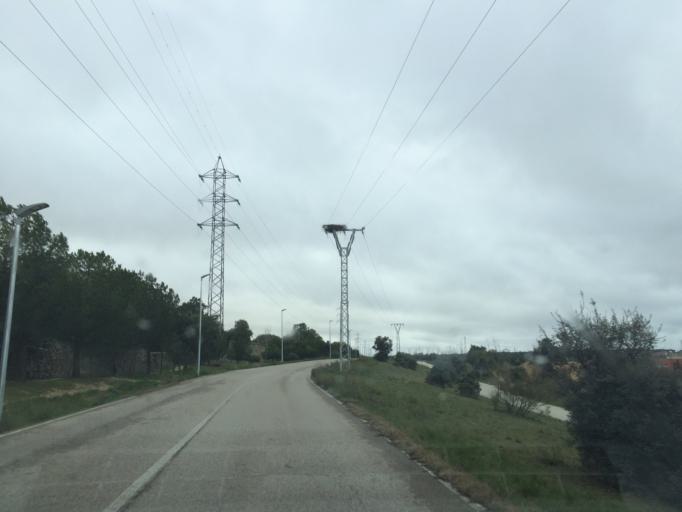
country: ES
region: Madrid
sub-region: Provincia de Madrid
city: Tres Cantos
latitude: 40.5984
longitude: -3.6918
